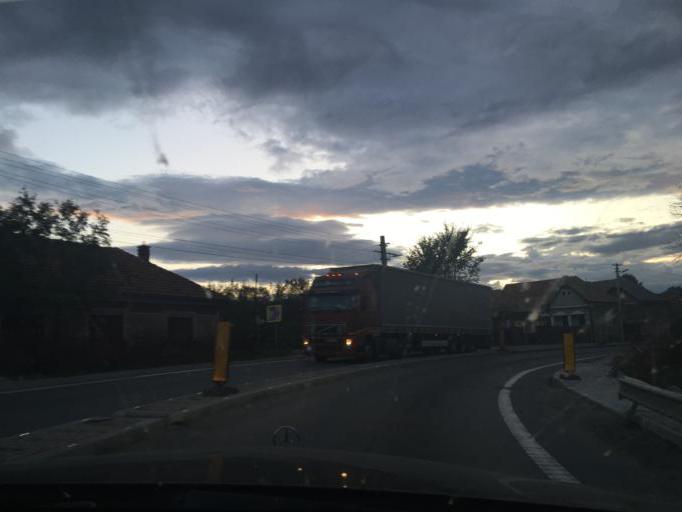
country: RO
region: Cluj
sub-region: Comuna Aghiresu
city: Aghiresu
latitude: 46.8139
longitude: 23.1827
